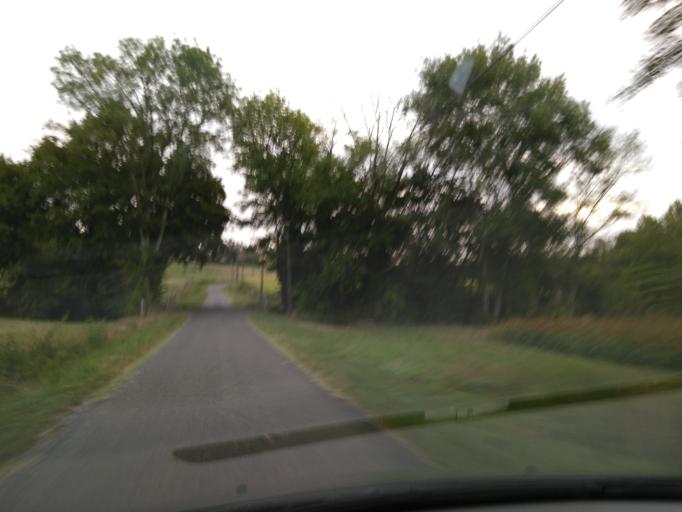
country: FR
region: Aquitaine
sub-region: Departement du Lot-et-Garonne
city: Saint-Hilaire
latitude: 44.5045
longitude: 0.6798
